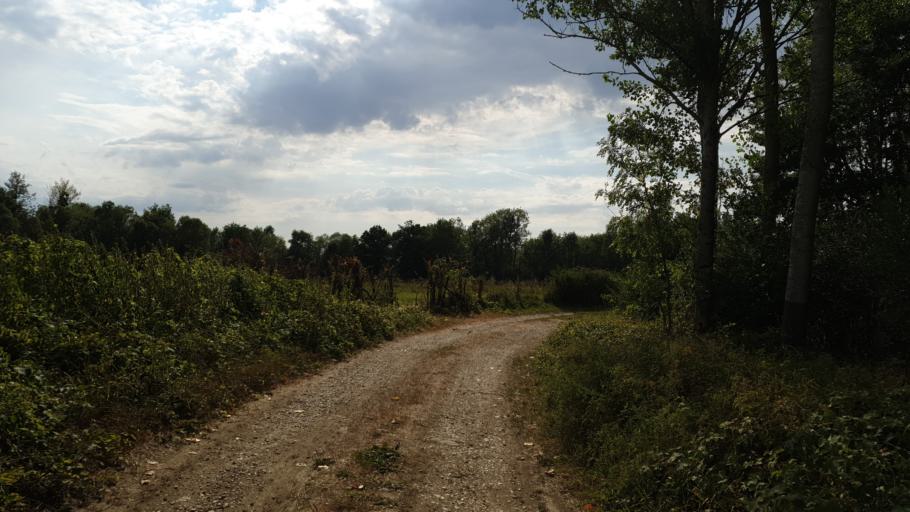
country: FR
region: Champagne-Ardenne
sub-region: Departement de la Marne
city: Pargny-sur-Saulx
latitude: 48.7643
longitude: 4.7490
